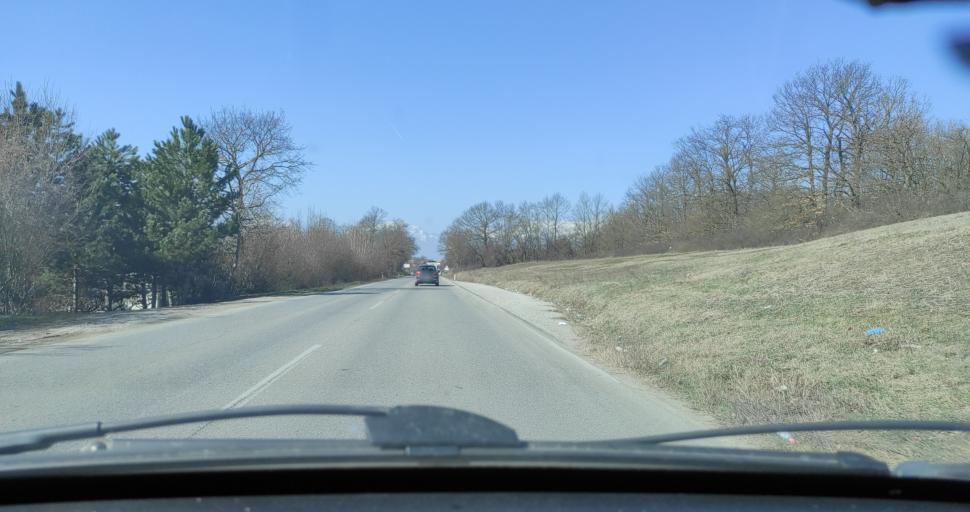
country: XK
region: Pec
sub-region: Komuna e Pejes
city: Kosuriq
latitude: 42.6210
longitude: 20.4778
